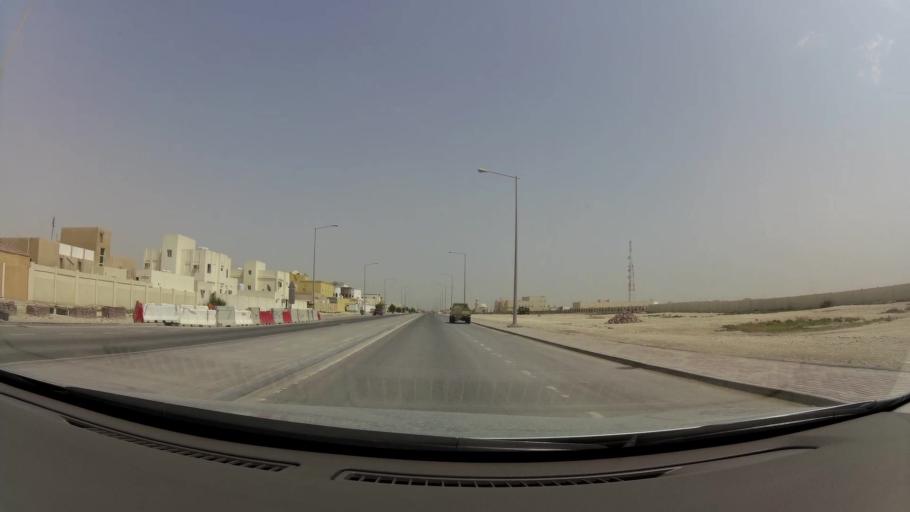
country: QA
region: Baladiyat ar Rayyan
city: Ar Rayyan
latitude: 25.2264
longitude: 51.4130
